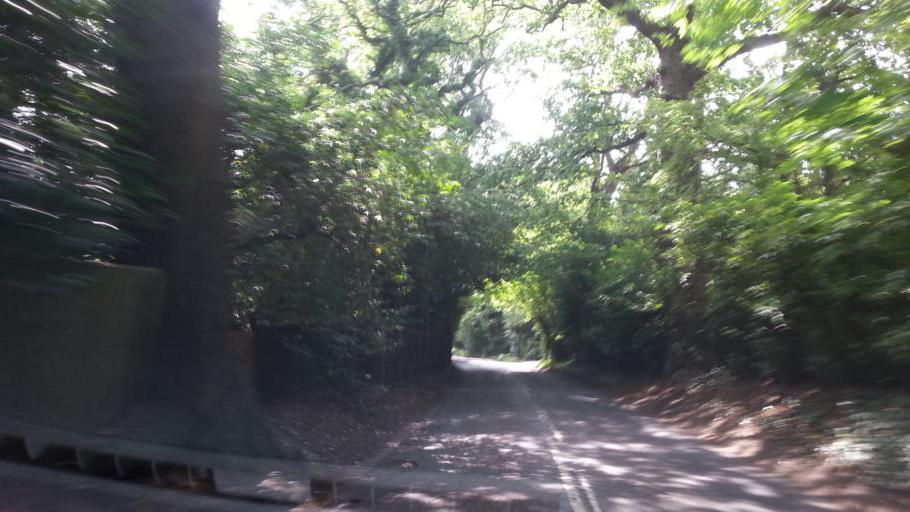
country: GB
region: England
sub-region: Surrey
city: Chobham
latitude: 51.3408
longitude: -0.5802
